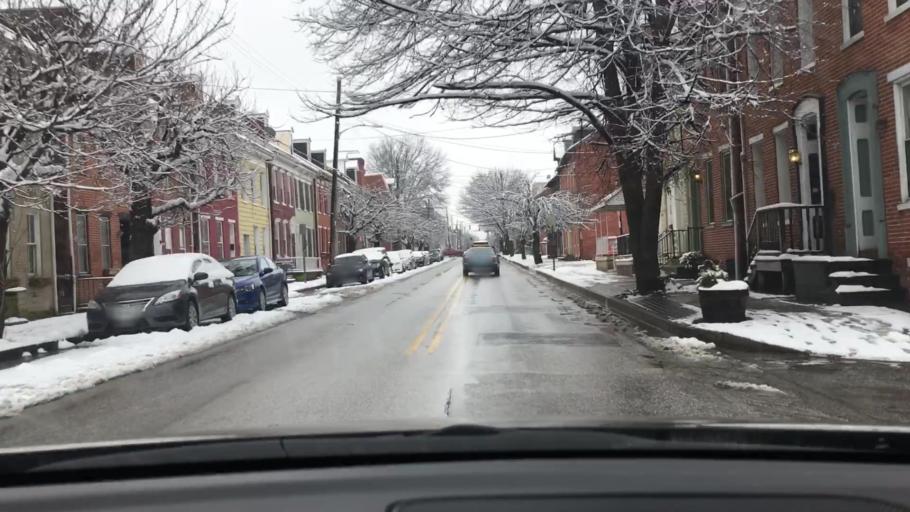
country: US
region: Pennsylvania
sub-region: York County
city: York
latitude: 39.9574
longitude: -76.7338
